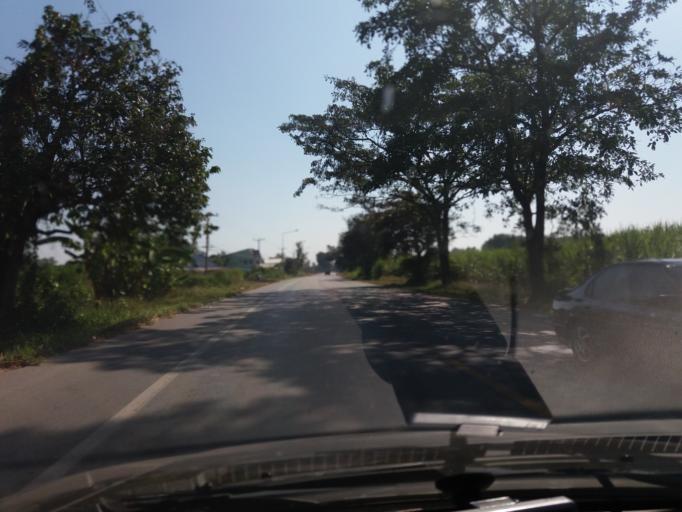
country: TH
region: Kamphaeng Phet
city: Khlong Khlung
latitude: 16.2067
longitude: 99.7563
